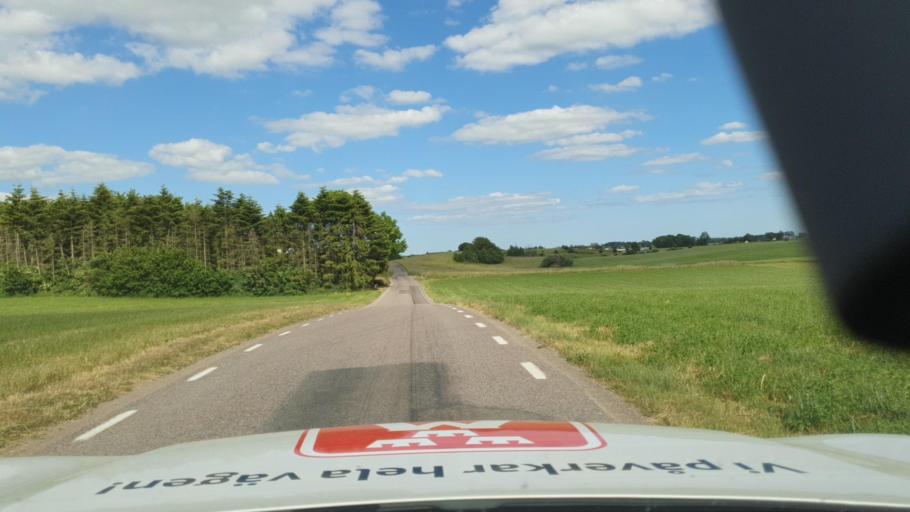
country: SE
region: Skane
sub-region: Ystads Kommun
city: Kopingebro
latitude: 55.4698
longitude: 13.9617
